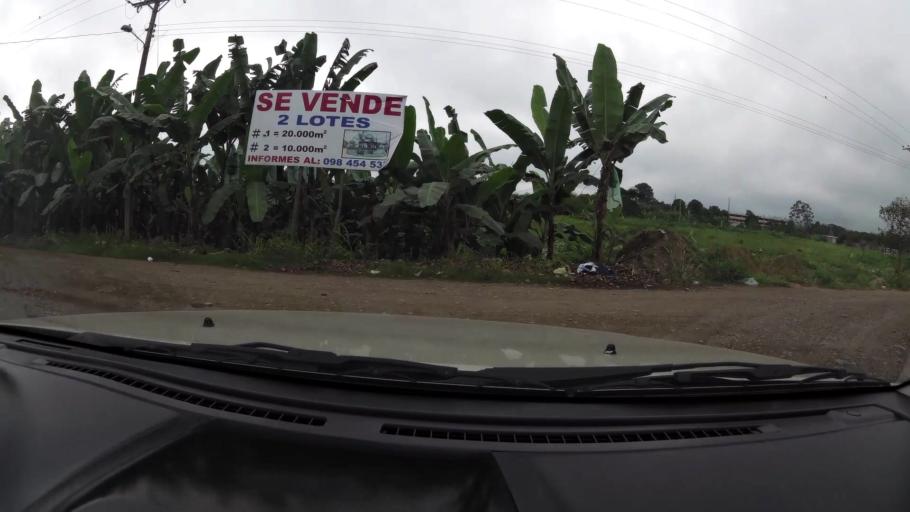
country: EC
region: El Oro
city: Pasaje
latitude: -3.3201
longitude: -79.8105
